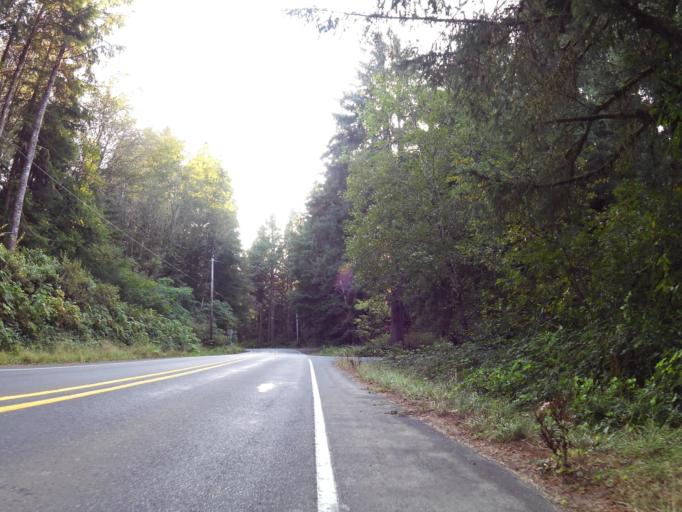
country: US
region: Oregon
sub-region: Lincoln County
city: Lincoln City
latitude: 44.9652
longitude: -123.9959
